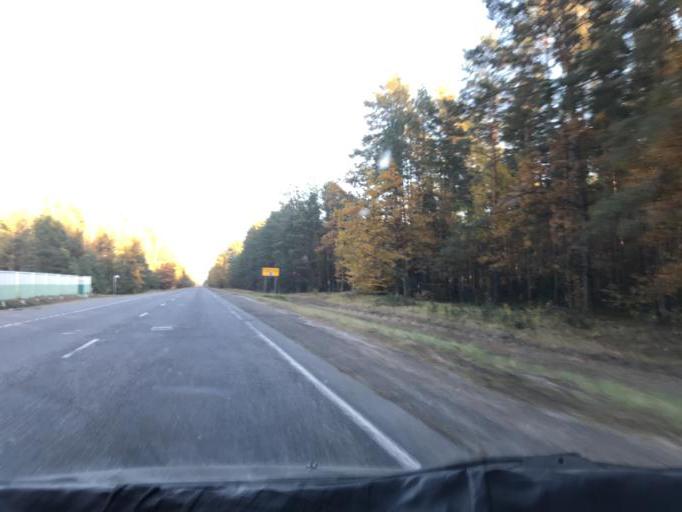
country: BY
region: Gomel
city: Zhytkavichy
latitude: 52.2748
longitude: 28.1826
